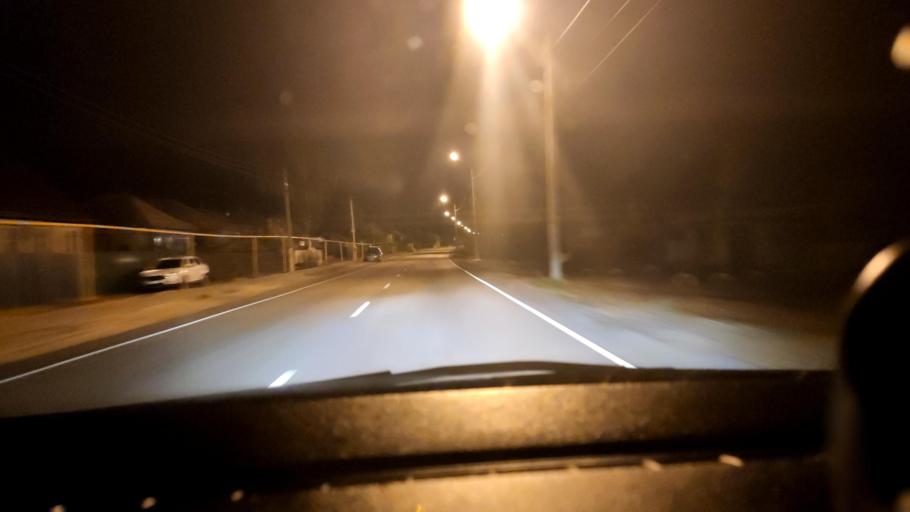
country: RU
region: Voronezj
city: Shilovo
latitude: 51.5635
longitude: 39.0536
